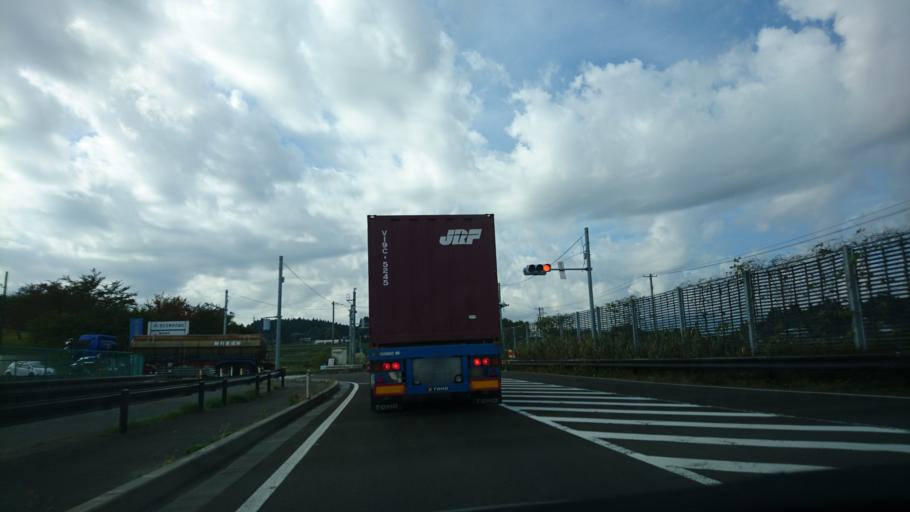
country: JP
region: Miyagi
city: Furukawa
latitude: 38.5100
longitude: 140.8943
